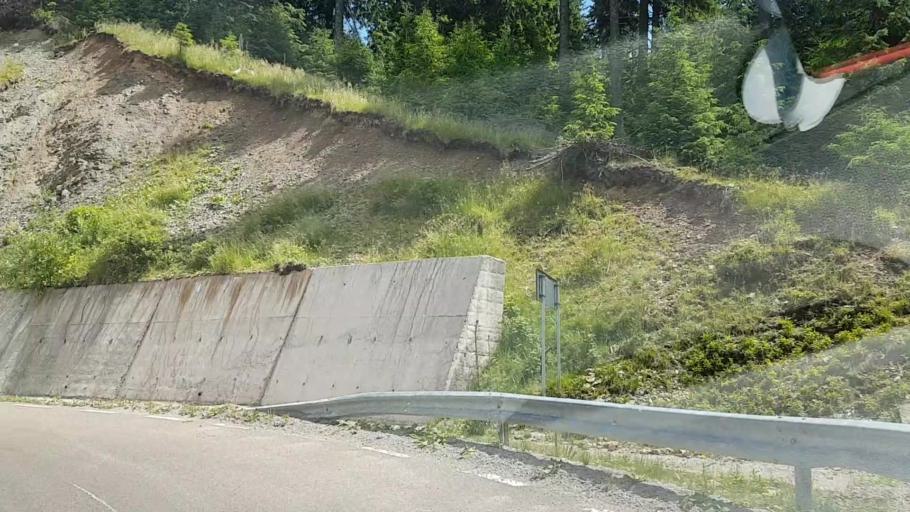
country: RO
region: Suceava
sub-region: Comuna Sadova
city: Sadova
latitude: 47.4577
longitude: 25.5297
